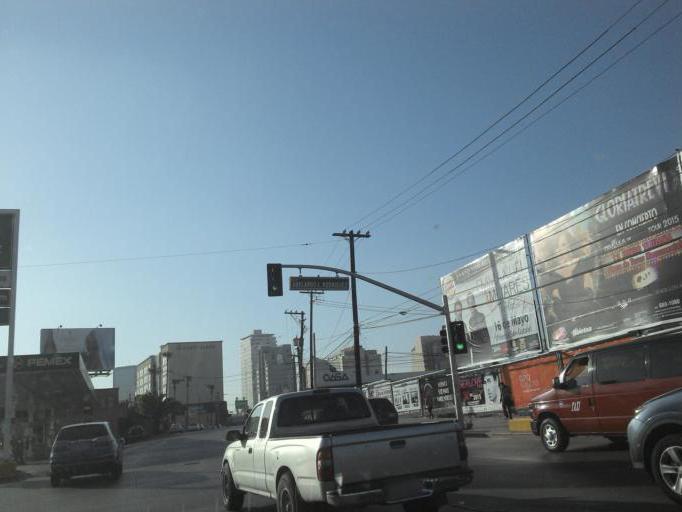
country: MX
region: Baja California
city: Tijuana
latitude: 32.5169
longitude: -117.0137
